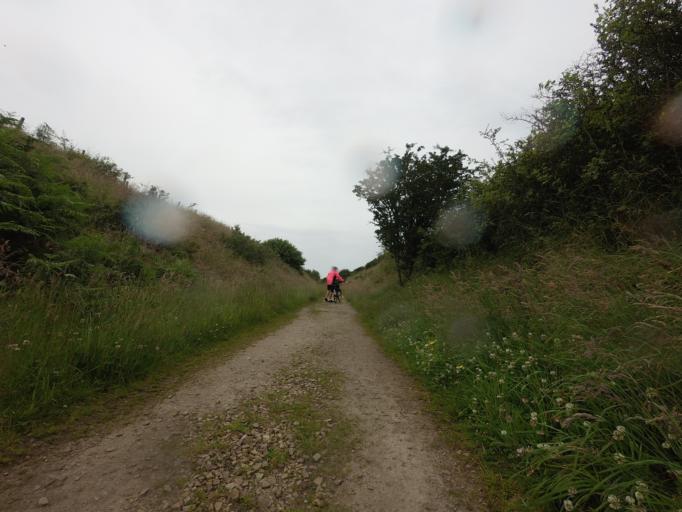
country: GB
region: Scotland
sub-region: Moray
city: Portknockie
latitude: 57.6983
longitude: -2.8507
